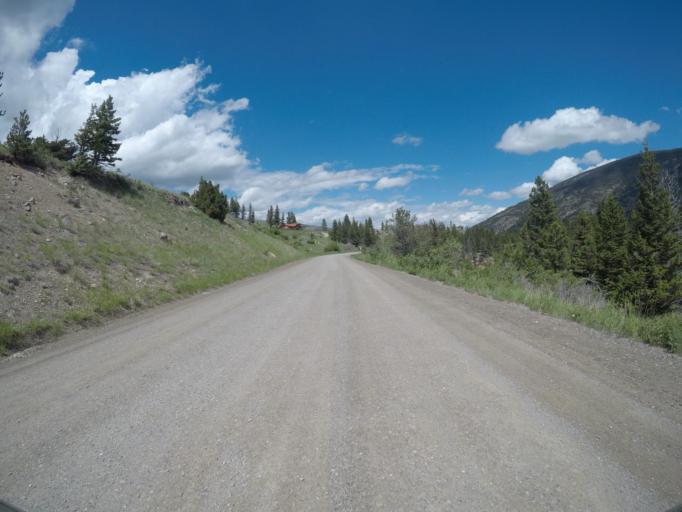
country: US
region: Montana
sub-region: Park County
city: Livingston
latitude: 45.5483
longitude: -110.2109
